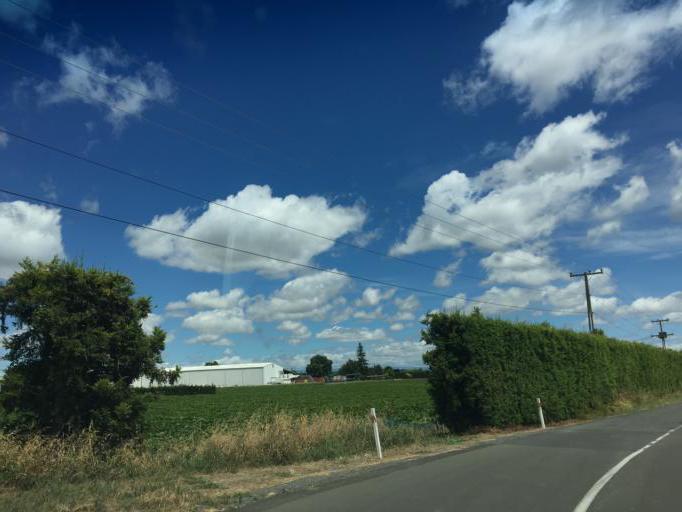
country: NZ
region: Hawke's Bay
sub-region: Hastings District
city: Hastings
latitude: -39.6564
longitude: 176.8916
